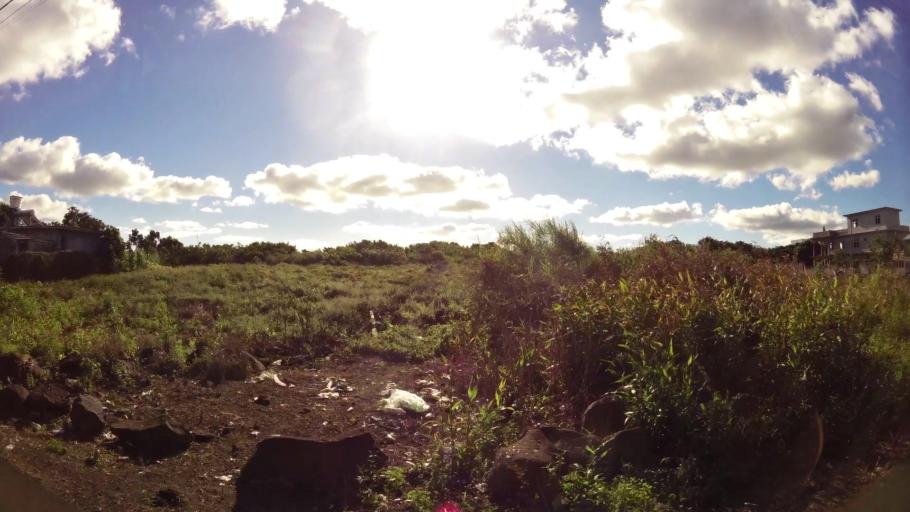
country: MU
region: Plaines Wilhems
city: Curepipe
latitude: -20.2885
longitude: 57.5177
